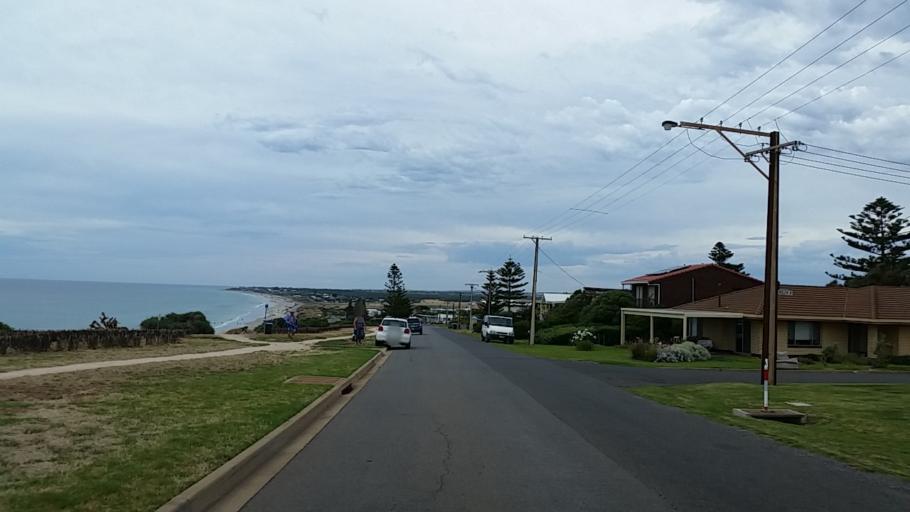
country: AU
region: South Australia
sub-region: Onkaparinga
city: Port Willunga
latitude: -35.3371
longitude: 138.4476
